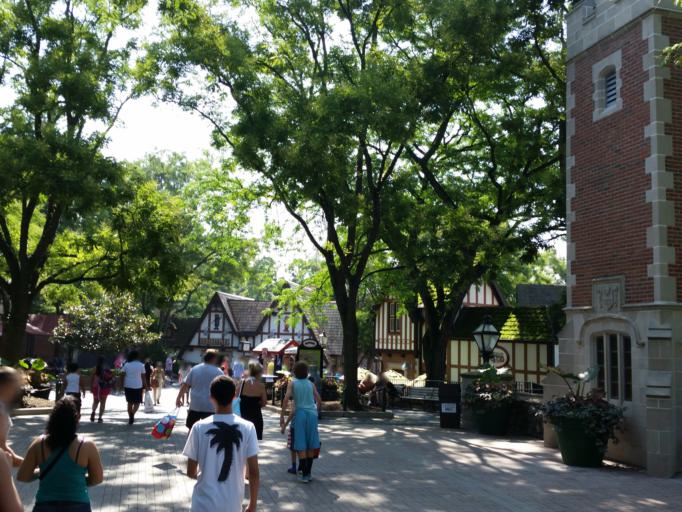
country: US
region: Pennsylvania
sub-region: Dauphin County
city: Hershey
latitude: 40.2876
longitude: -76.6590
